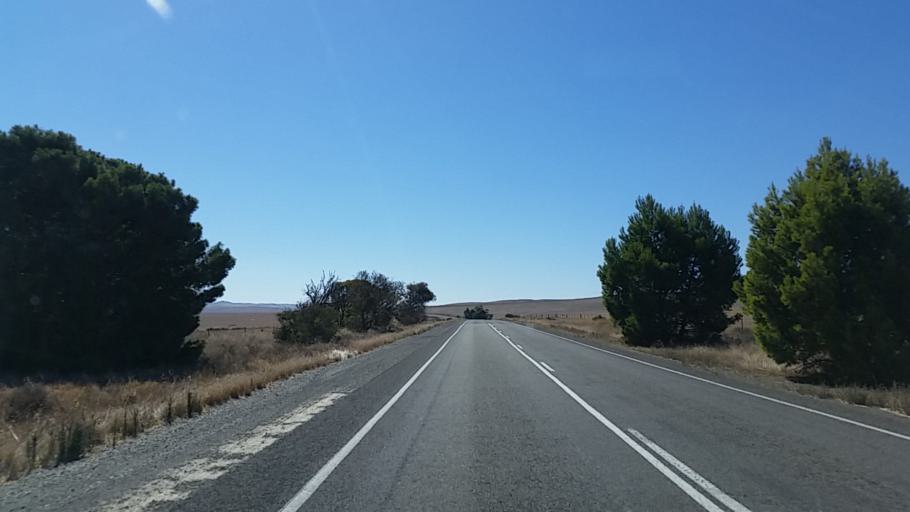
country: AU
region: South Australia
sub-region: Northern Areas
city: Jamestown
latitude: -33.3176
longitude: 138.8831
